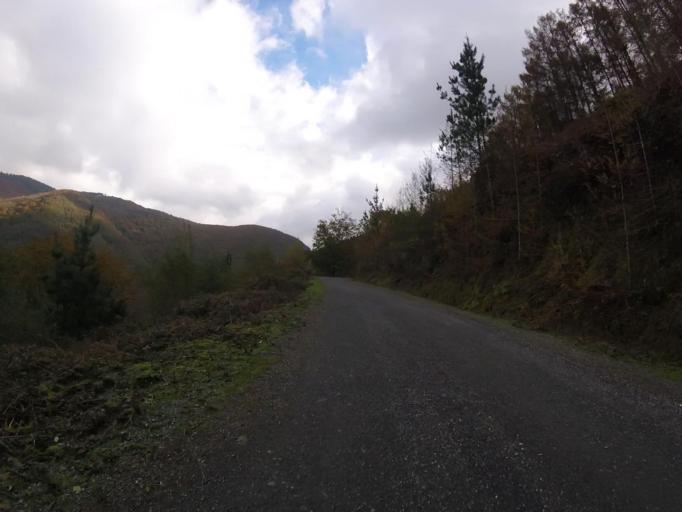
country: ES
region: Navarre
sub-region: Provincia de Navarra
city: Goizueta
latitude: 43.2252
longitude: -1.8265
